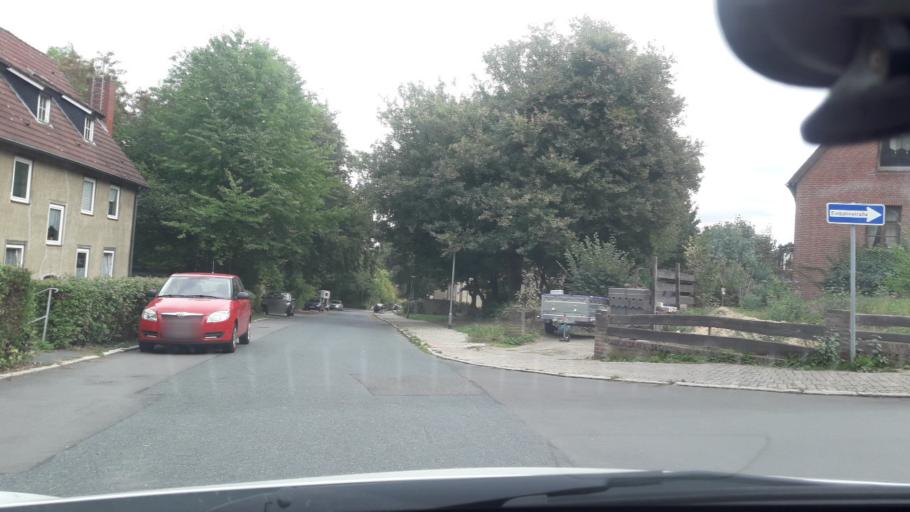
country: DE
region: Lower Saxony
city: Elbe
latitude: 52.1068
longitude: 10.3446
